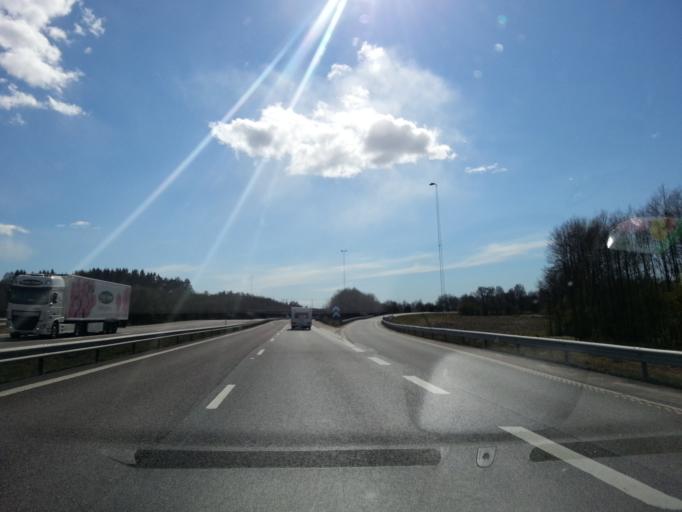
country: SE
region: Vaestra Goetaland
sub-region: Stenungsunds Kommun
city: Stenungsund
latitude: 58.0601
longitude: 11.8827
